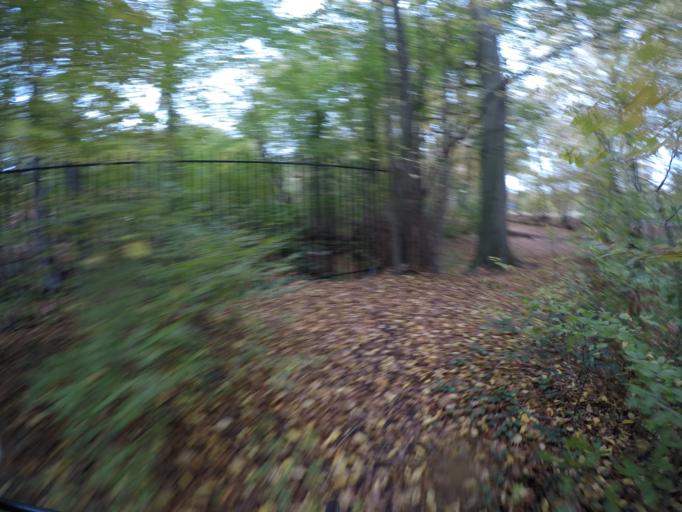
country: BE
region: Flanders
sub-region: Provincie Antwerpen
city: Schoten
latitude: 51.2271
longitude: 4.4885
